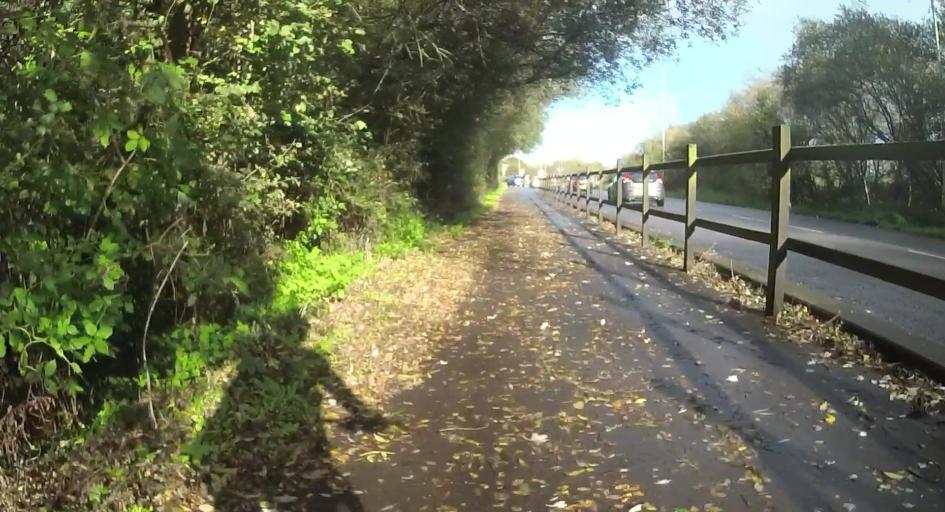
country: GB
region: England
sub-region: Wokingham
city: Lower Earley
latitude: 51.4278
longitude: -0.9010
